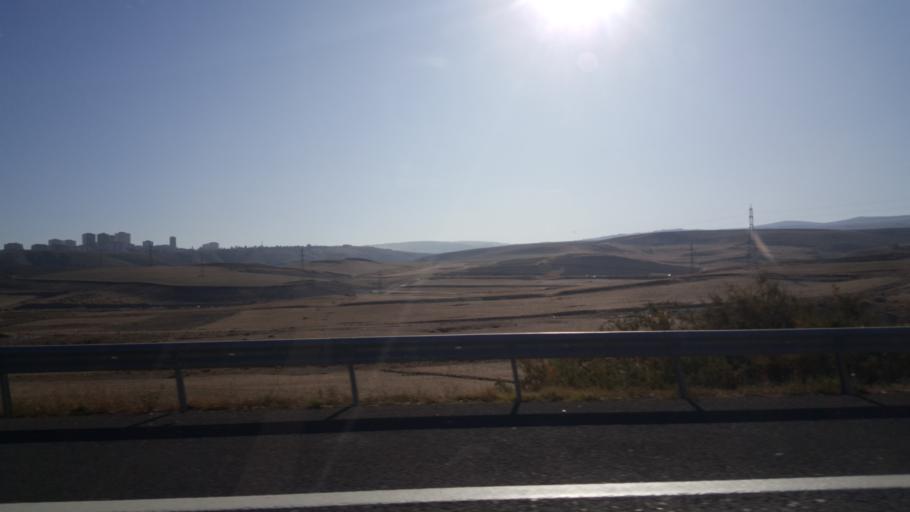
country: TR
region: Ankara
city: Mamak
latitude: 39.8903
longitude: 32.9567
